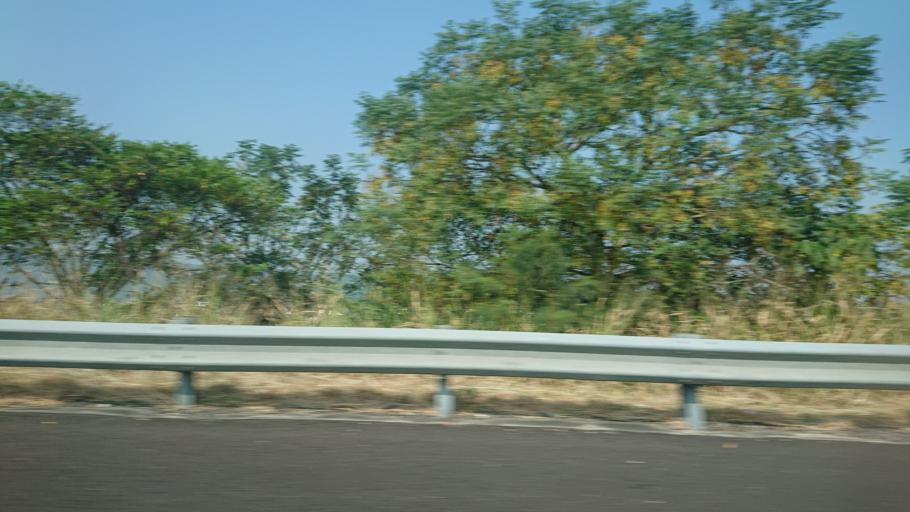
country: TW
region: Taiwan
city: Lugu
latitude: 23.8142
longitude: 120.6994
